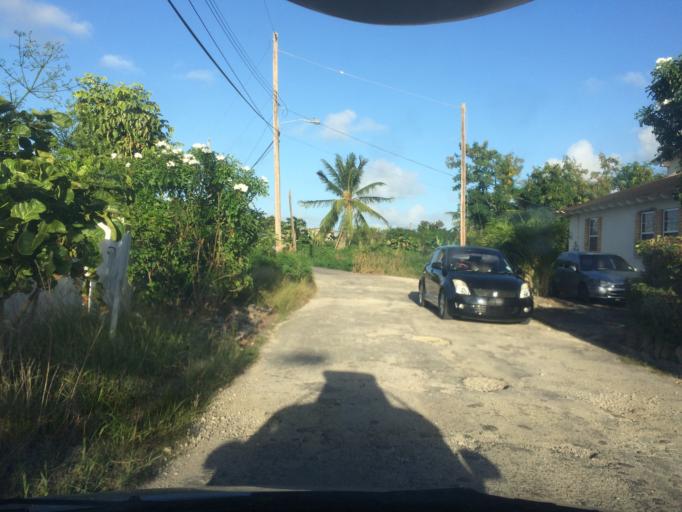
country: BB
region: Saint Lucy
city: Checker Hall
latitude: 13.2958
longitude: -59.6454
